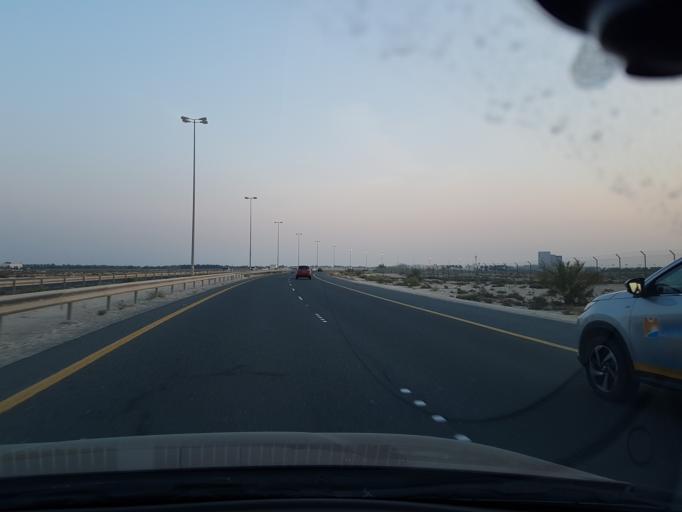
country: BH
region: Central Governorate
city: Dar Kulayb
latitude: 26.0337
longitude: 50.4998
